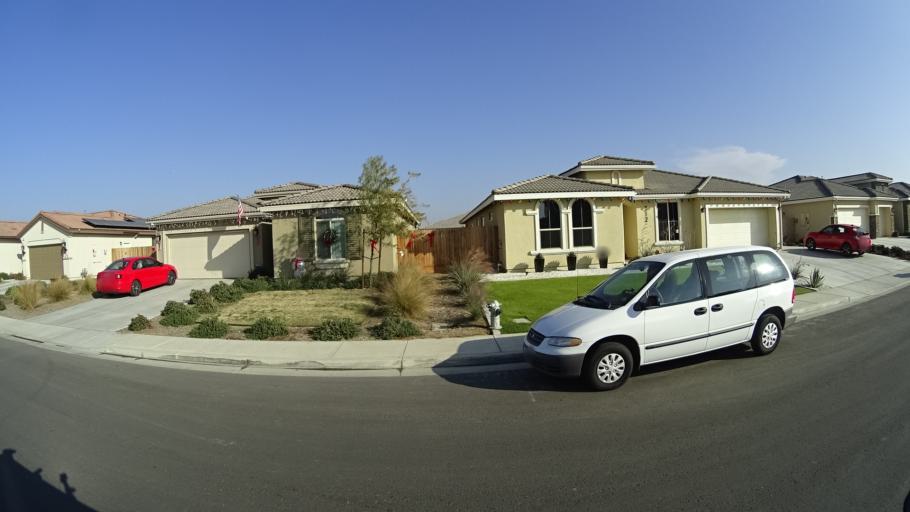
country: US
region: California
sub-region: Kern County
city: Rosedale
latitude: 35.3519
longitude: -119.1726
